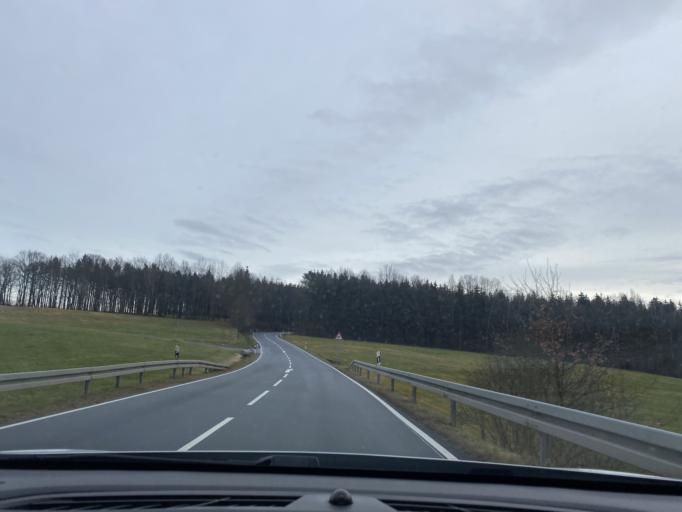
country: DE
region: Saxony
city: Reichenbach
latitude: 51.1163
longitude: 14.8361
